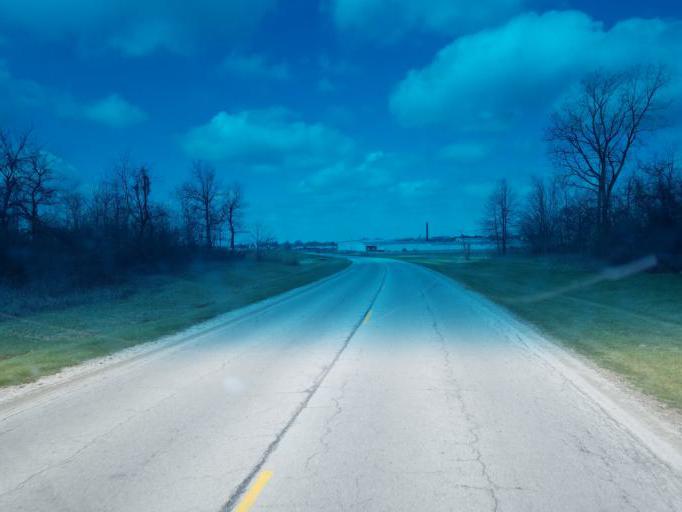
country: US
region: Ohio
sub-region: Crawford County
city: Bucyrus
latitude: 40.7901
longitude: -82.9628
